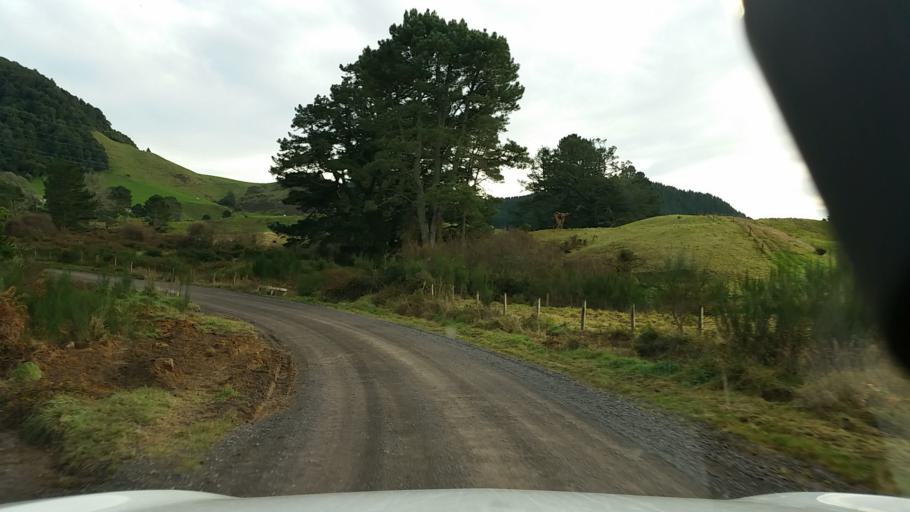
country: NZ
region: Bay of Plenty
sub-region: Rotorua District
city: Rotorua
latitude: -38.2352
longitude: 176.1652
